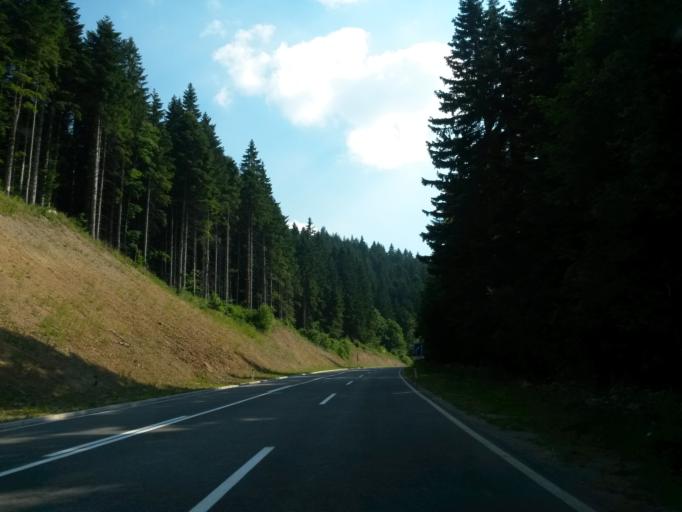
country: BA
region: Federation of Bosnia and Herzegovina
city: Bugojno
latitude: 44.0182
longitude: 17.2906
